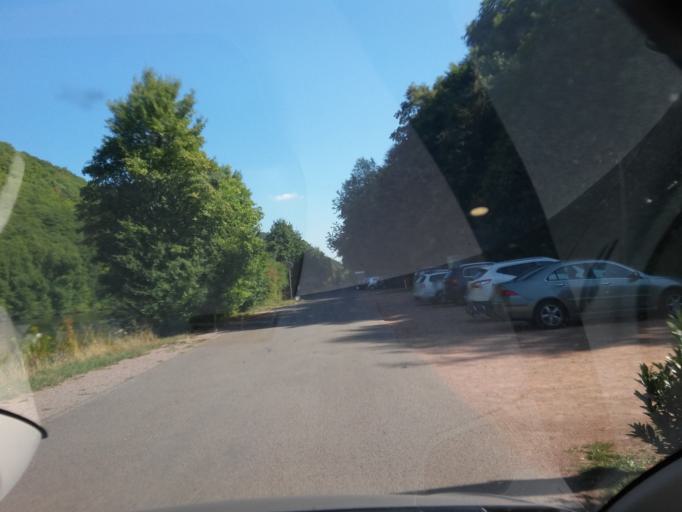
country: DE
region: Saarland
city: Orscholz
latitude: 49.4956
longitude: 6.5502
